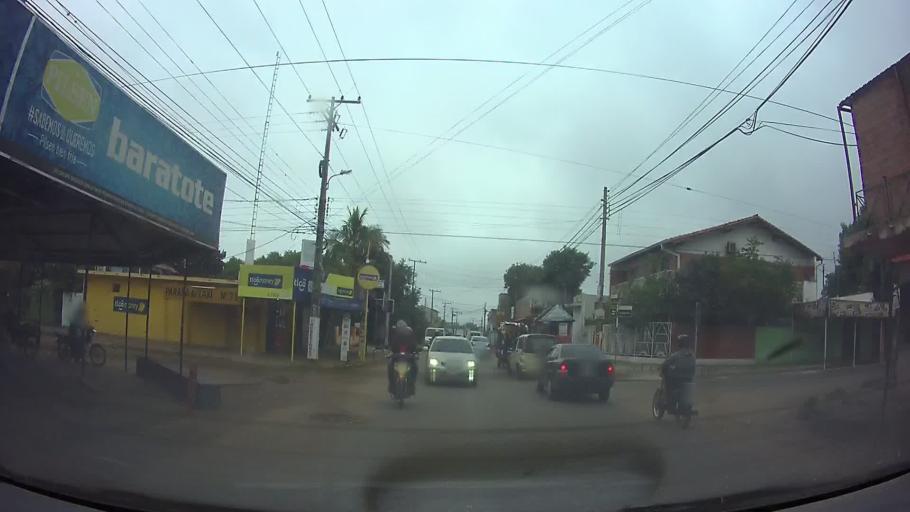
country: PY
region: Central
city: San Lorenzo
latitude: -25.3221
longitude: -57.4978
